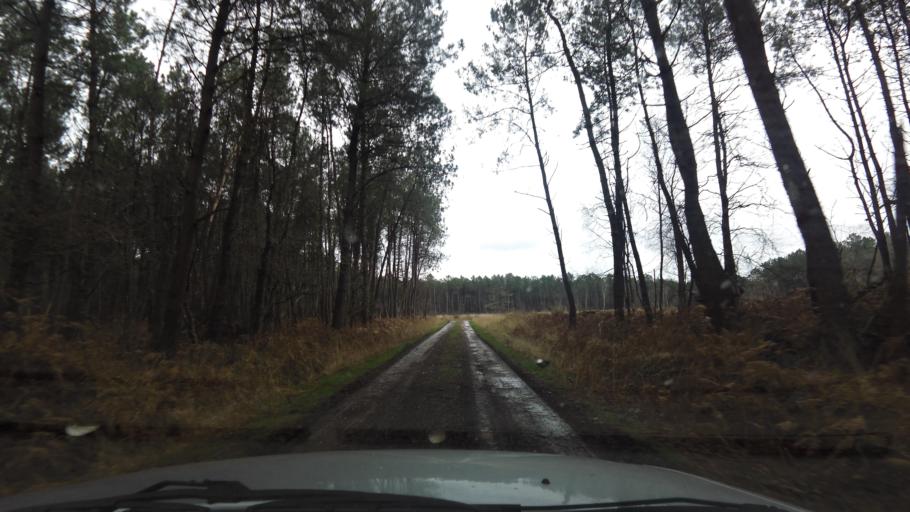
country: FR
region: Brittany
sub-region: Departement du Morbihan
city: Molac
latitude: 47.7662
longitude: -2.4803
